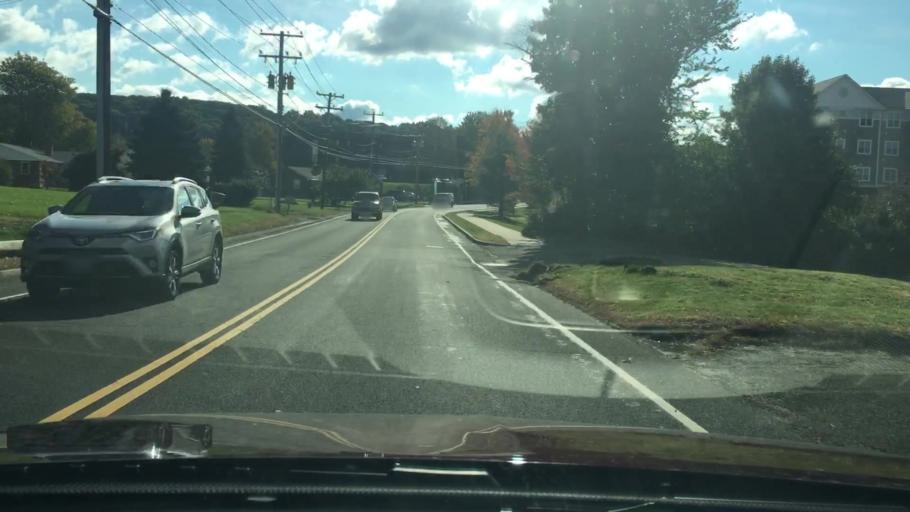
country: US
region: Connecticut
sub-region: New Haven County
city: Meriden
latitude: 41.5225
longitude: -72.7651
